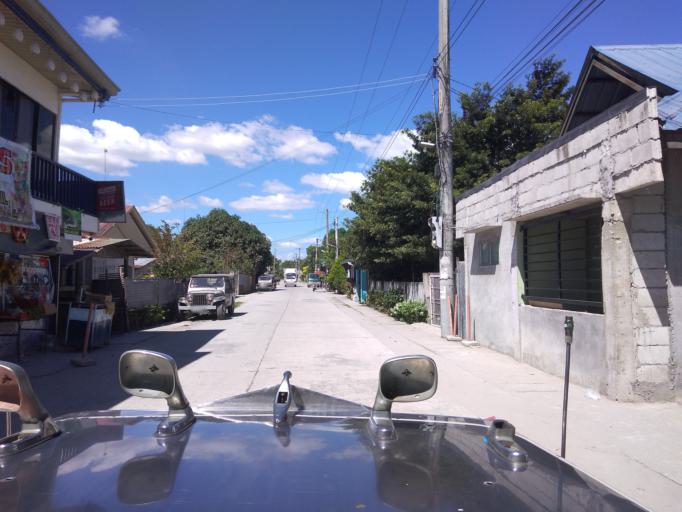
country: PH
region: Central Luzon
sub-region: Province of Pampanga
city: Magliman
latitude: 15.0337
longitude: 120.6484
